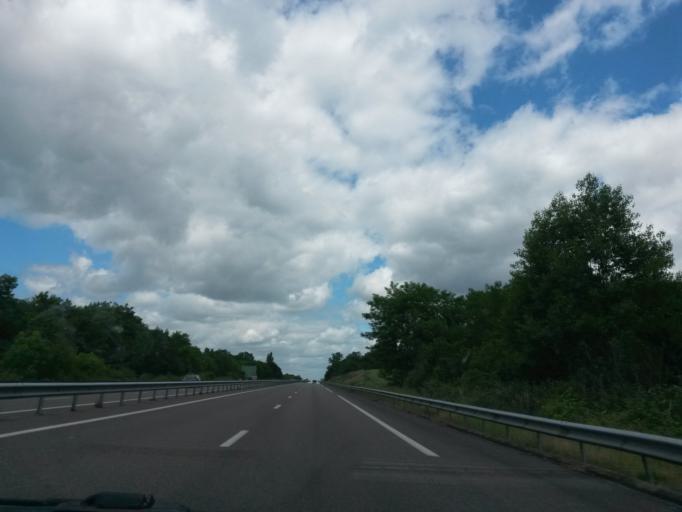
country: FR
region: Bourgogne
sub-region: Departement de la Nievre
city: Cosne-Cours-sur-Loire
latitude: 47.3656
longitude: 2.9234
